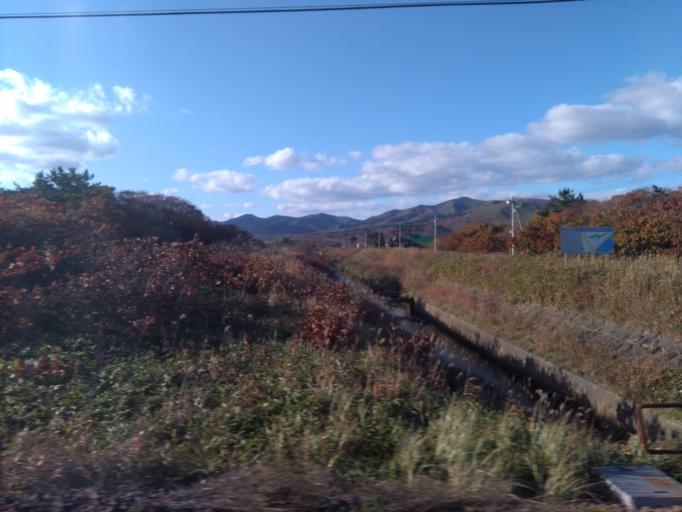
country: JP
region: Hokkaido
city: Niseko Town
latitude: 42.5532
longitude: 140.4210
